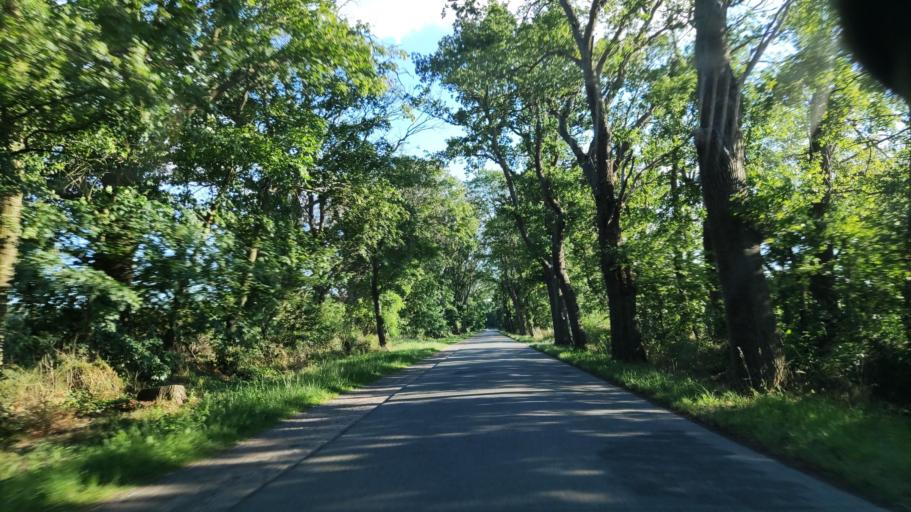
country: DE
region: Lower Saxony
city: Gartow
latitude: 53.0283
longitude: 11.4881
